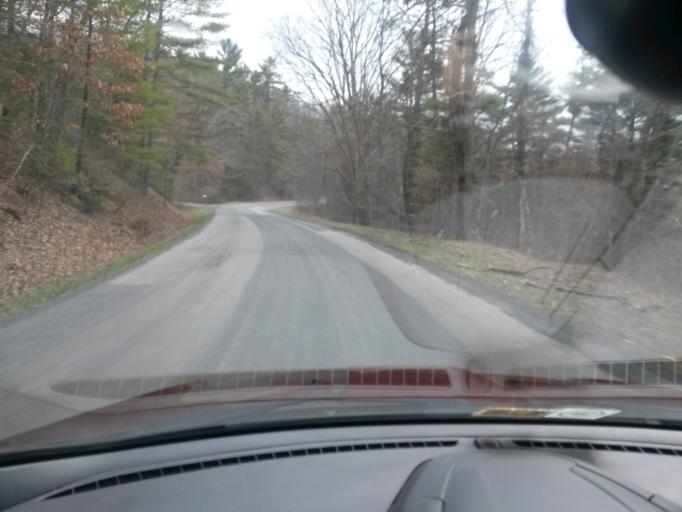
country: US
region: Virginia
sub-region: Bath County
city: Warm Springs
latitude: 38.0616
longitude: -79.8340
